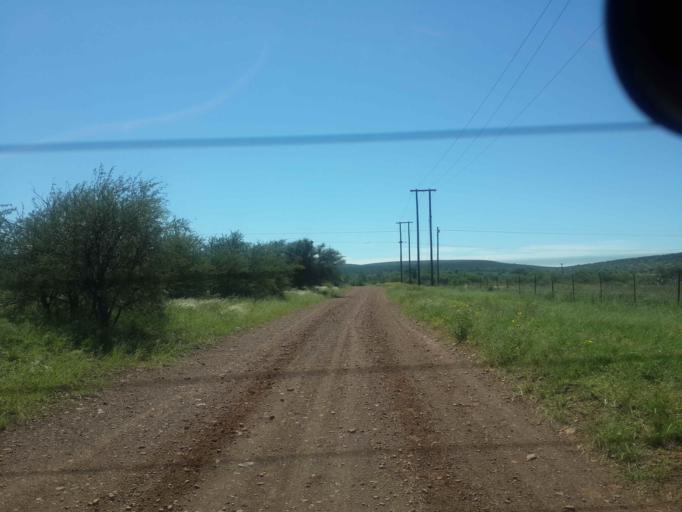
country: ZA
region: Northern Cape
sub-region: Siyanda District Municipality
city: Danielskuil
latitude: -28.1816
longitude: 23.5340
